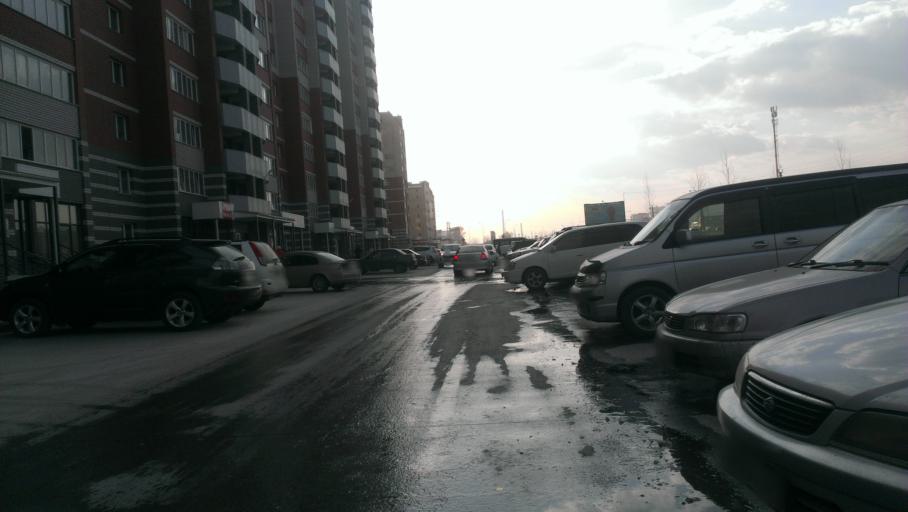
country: RU
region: Altai Krai
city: Novosilikatnyy
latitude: 53.3285
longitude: 83.6731
